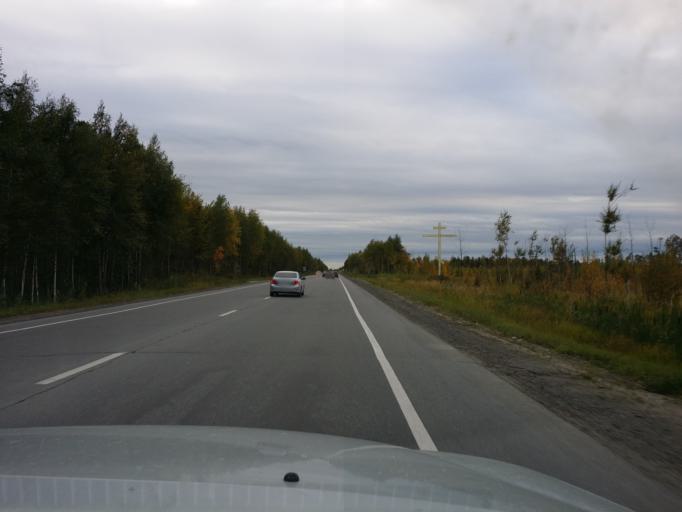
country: RU
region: Khanty-Mansiyskiy Avtonomnyy Okrug
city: Megion
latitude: 61.0622
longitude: 76.2767
